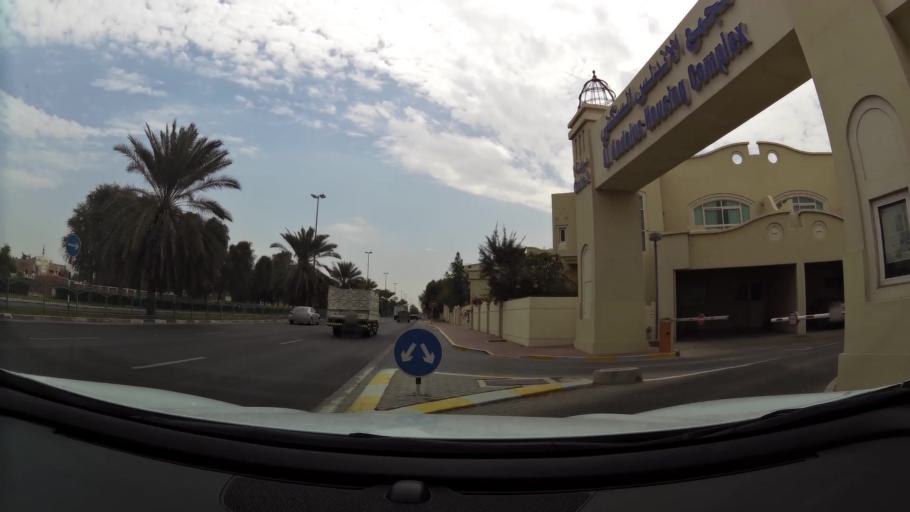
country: OM
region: Al Buraimi
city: Al Buraymi
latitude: 24.2189
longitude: 55.7856
